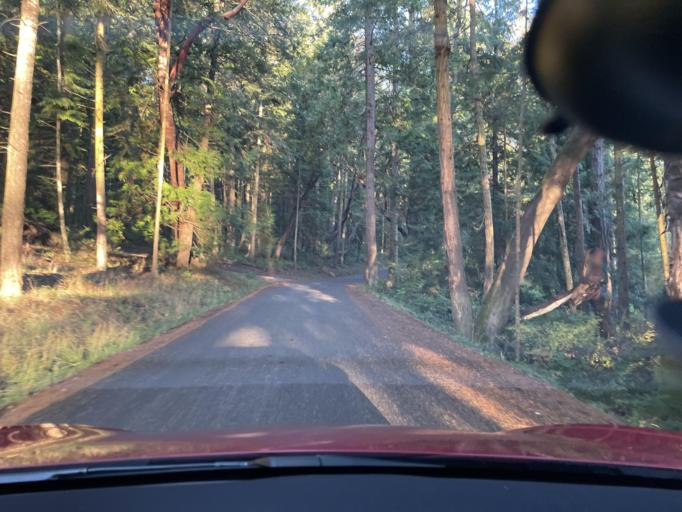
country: US
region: Washington
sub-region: San Juan County
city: Friday Harbor
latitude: 48.5999
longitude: -123.1561
